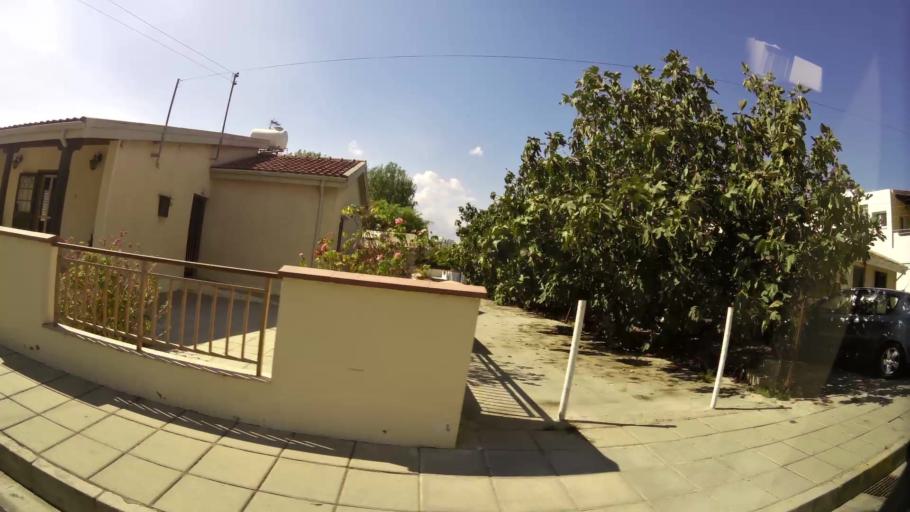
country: CY
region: Larnaka
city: Livadia
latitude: 34.9495
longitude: 33.6235
